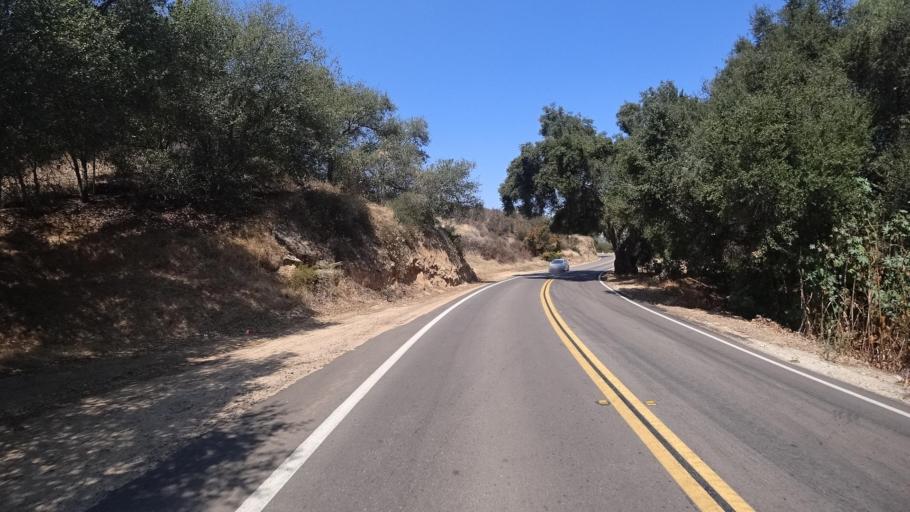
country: US
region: California
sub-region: San Diego County
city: Bonsall
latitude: 33.2674
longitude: -117.1695
